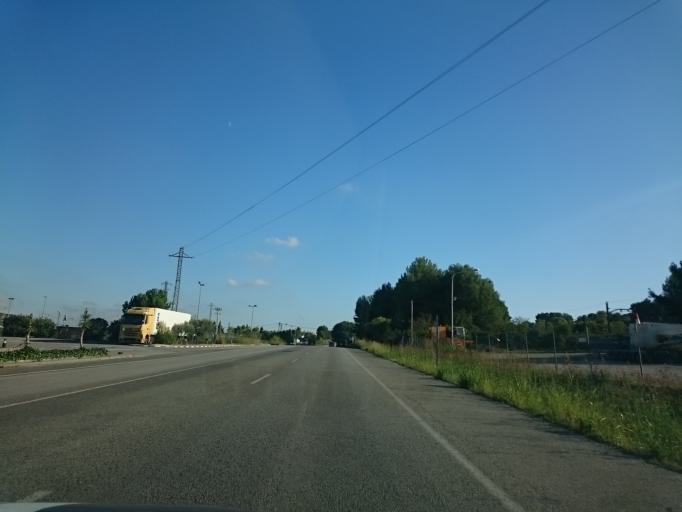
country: ES
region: Catalonia
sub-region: Provincia de Barcelona
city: Palleja
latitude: 41.4326
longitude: 1.9940
